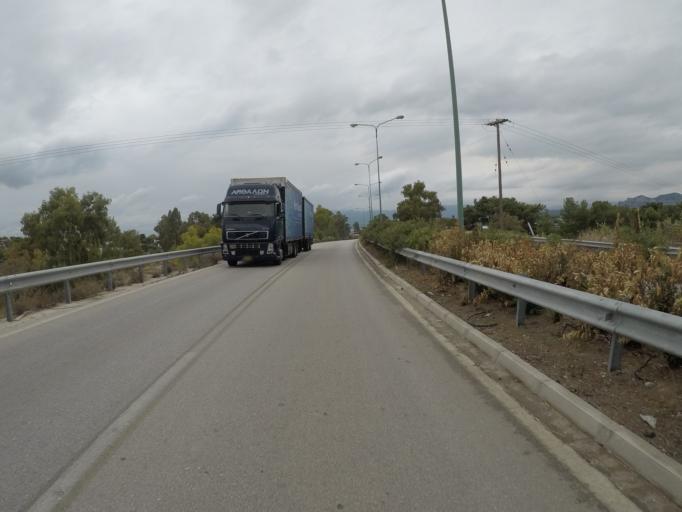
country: GR
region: Peloponnese
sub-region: Nomos Korinthias
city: Kyras Vrysi
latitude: 37.9303
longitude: 22.9941
